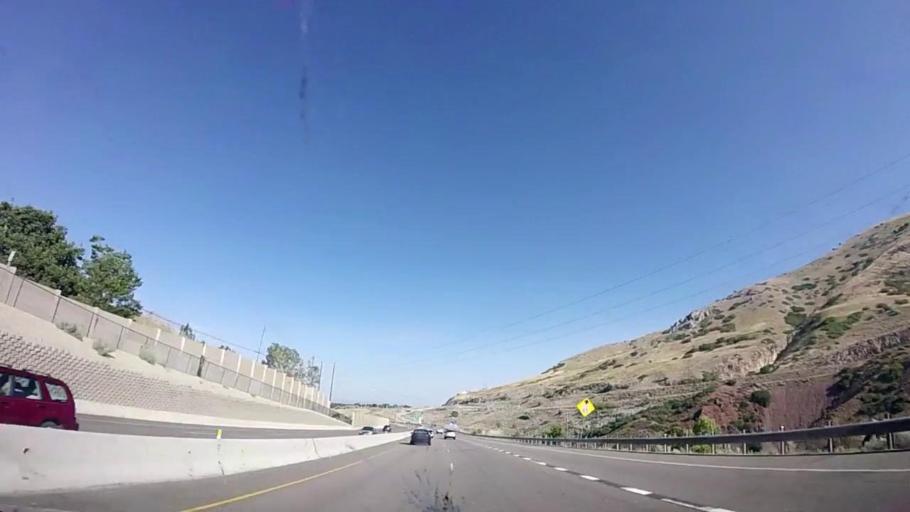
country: US
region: Utah
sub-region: Salt Lake County
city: East Millcreek
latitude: 40.7079
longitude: -111.7976
